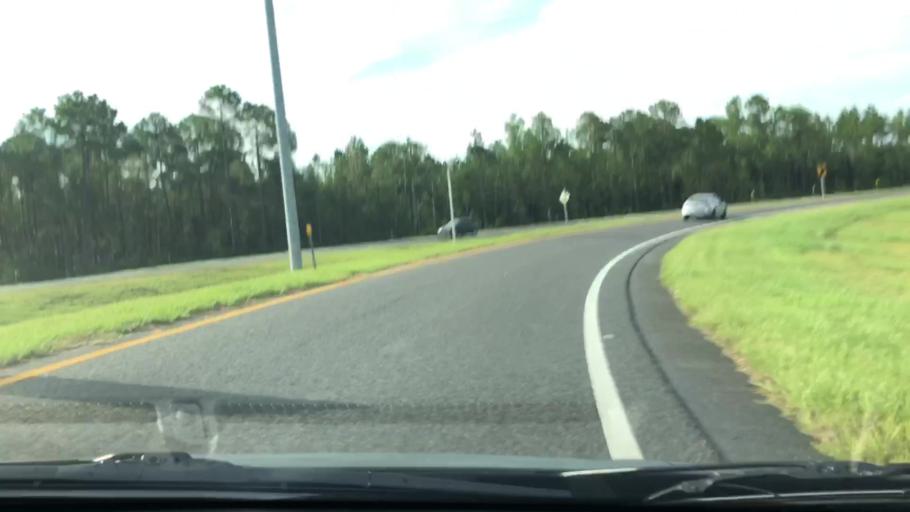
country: US
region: Florida
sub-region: Saint Johns County
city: Palm Valley
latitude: 30.1105
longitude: -81.4434
